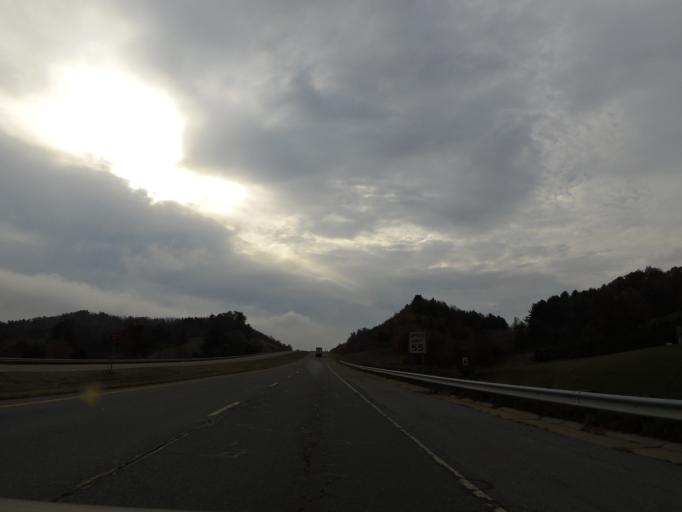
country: US
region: North Carolina
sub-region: Watauga County
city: Boone
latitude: 36.2428
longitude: -81.5399
